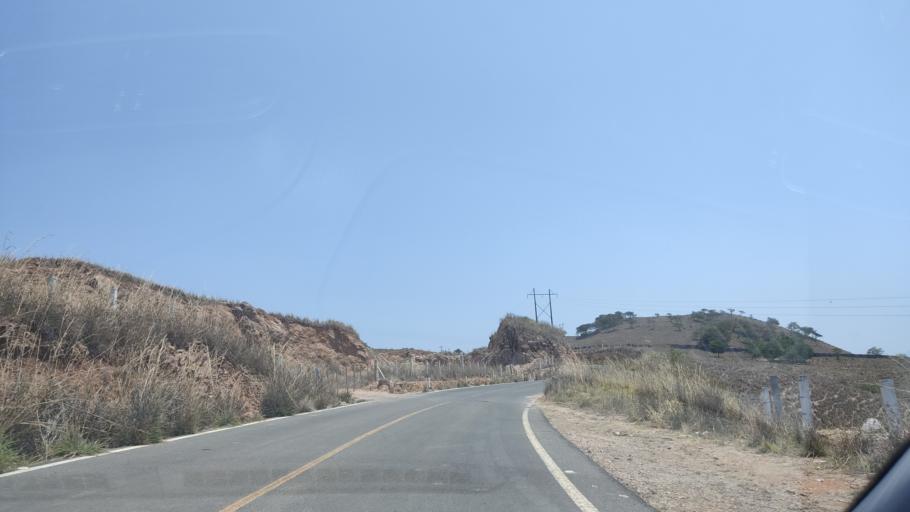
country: MX
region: Nayarit
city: Puga
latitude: 21.6105
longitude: -104.7341
